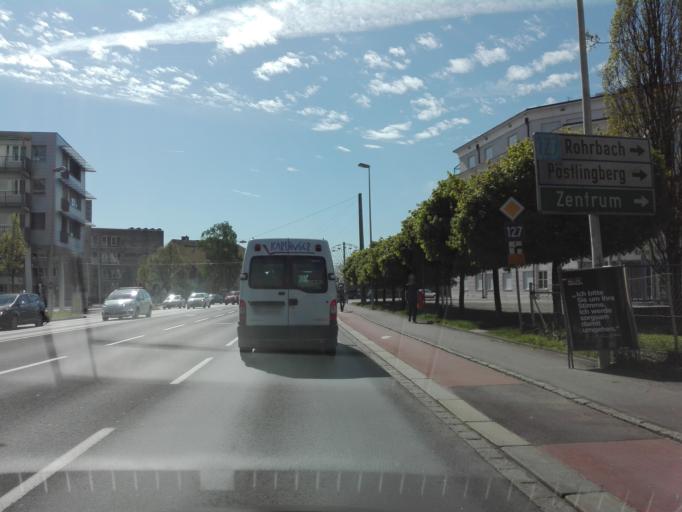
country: AT
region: Upper Austria
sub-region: Linz Stadt
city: Linz
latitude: 48.3139
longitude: 14.2859
